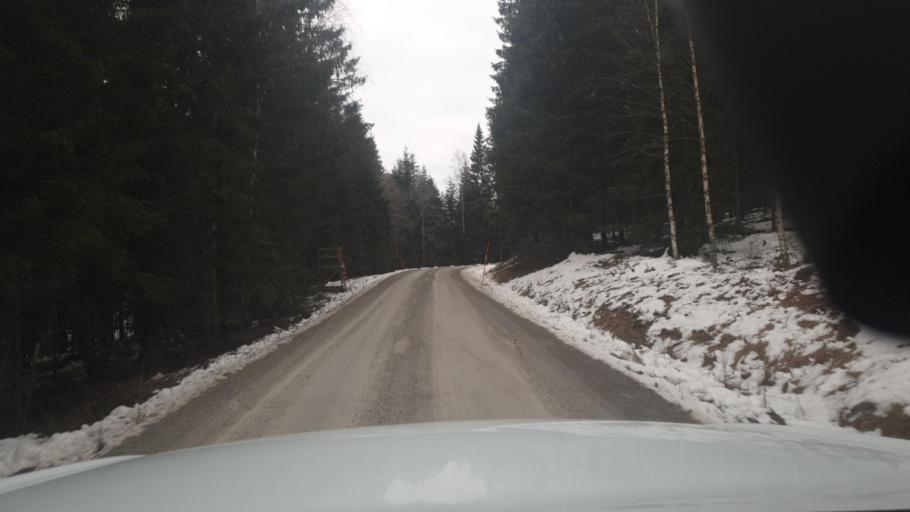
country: SE
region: Vaermland
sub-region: Sunne Kommun
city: Sunne
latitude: 59.8525
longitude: 12.9103
